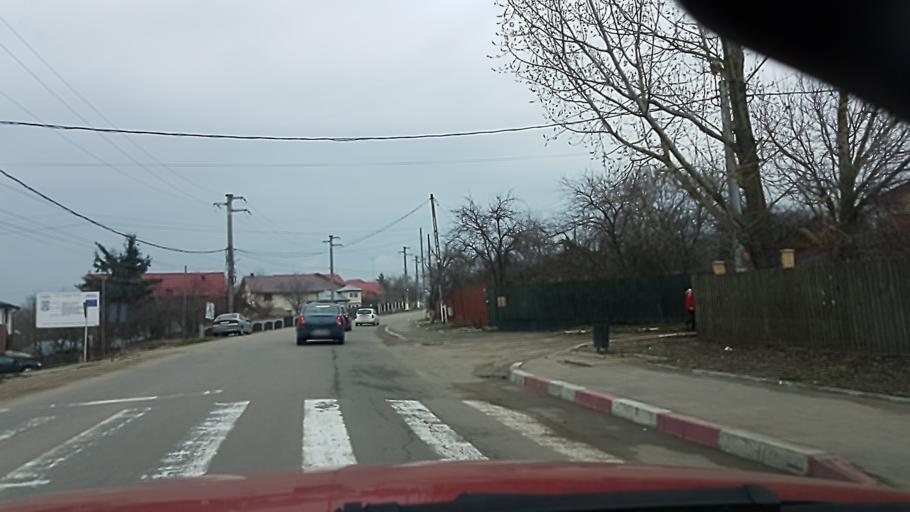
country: RO
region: Ilfov
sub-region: Comuna Balotesti
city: Balotesti
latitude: 44.6222
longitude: 26.1152
